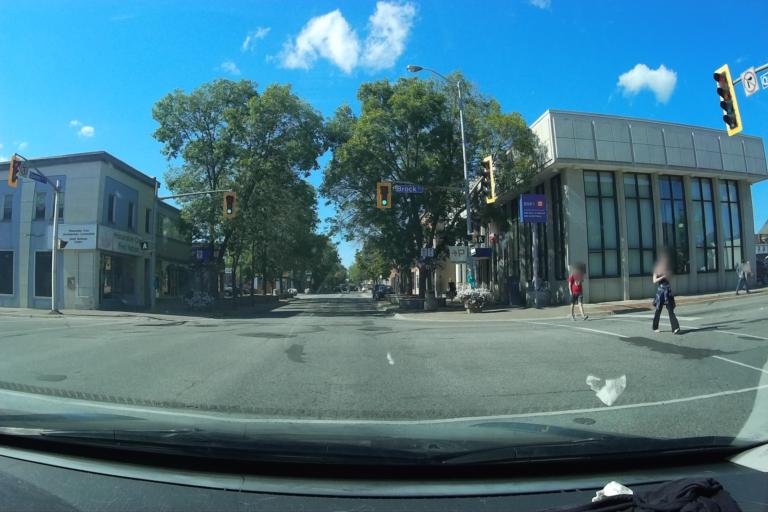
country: CA
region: Ontario
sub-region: Algoma
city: Sault Ste. Marie
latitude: 46.5091
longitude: -84.3298
